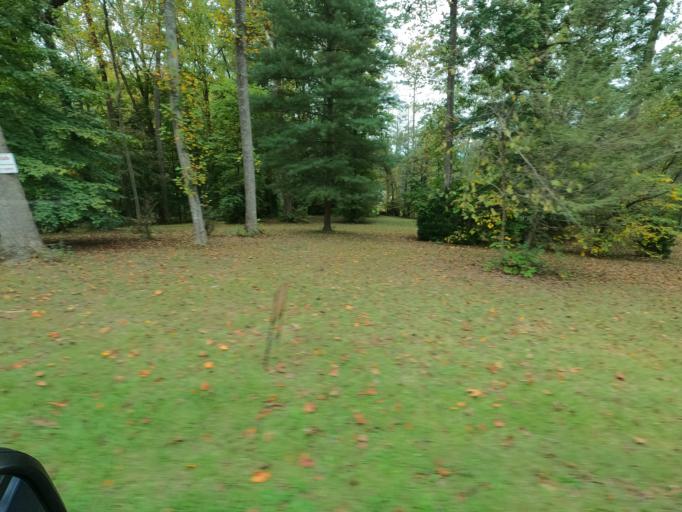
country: US
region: Tennessee
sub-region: Washington County
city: Jonesborough
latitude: 36.2303
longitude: -82.5620
